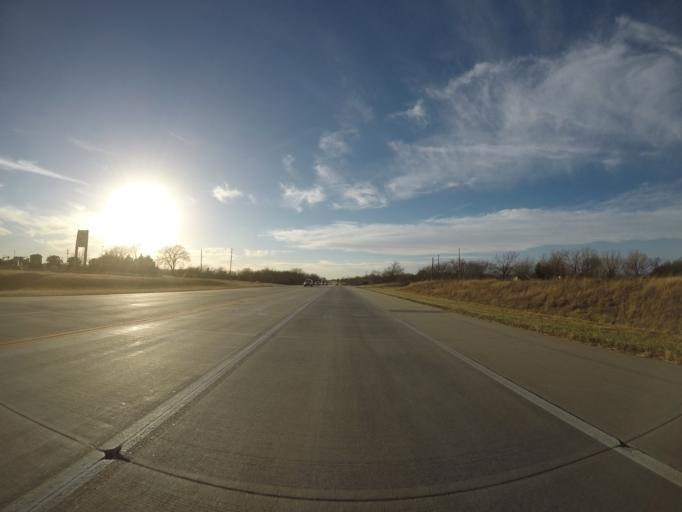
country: US
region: Kansas
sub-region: Lyon County
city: Emporia
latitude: 38.4124
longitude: -96.2615
